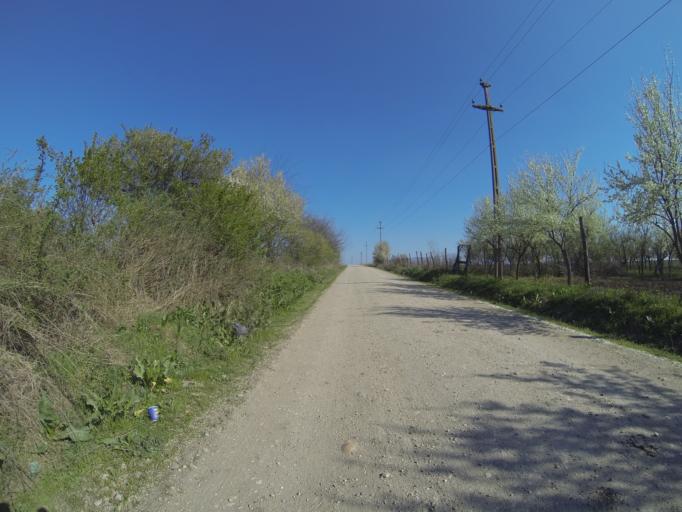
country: RO
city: Varvoru
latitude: 44.2231
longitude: 23.6352
